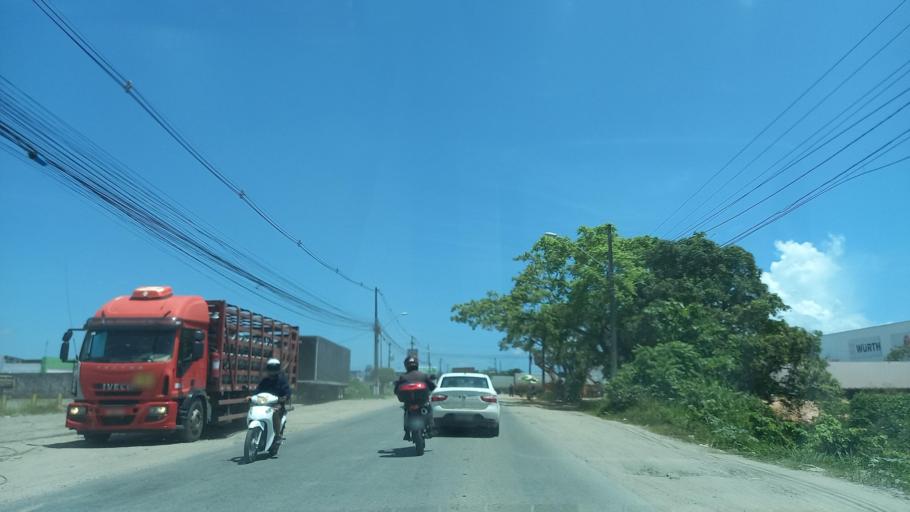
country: BR
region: Pernambuco
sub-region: Jaboatao Dos Guararapes
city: Jaboatao
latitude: -8.1556
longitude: -34.9641
